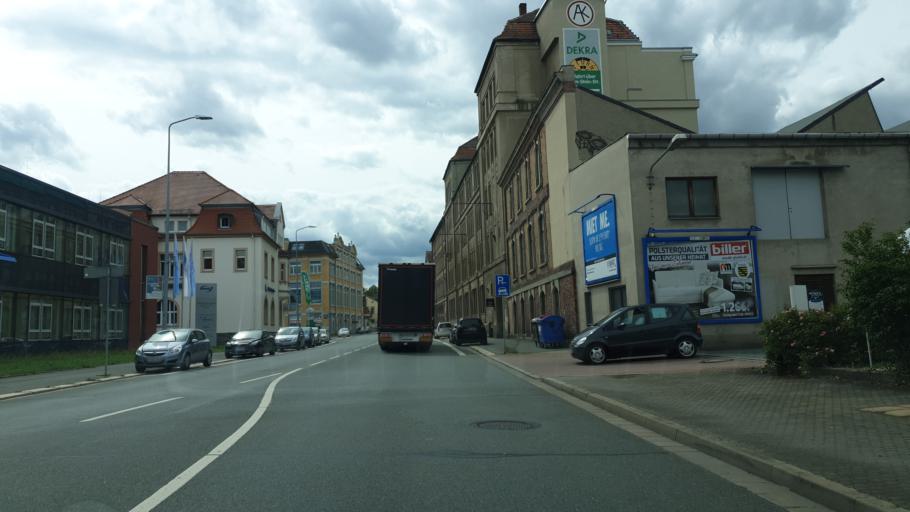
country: DE
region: Saxony
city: Plauen
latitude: 50.4995
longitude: 12.1475
